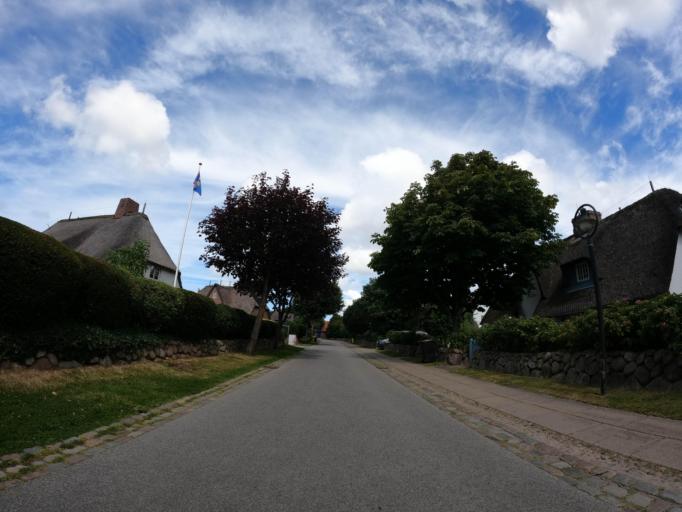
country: DE
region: Schleswig-Holstein
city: Keitum
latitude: 54.8907
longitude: 8.3706
